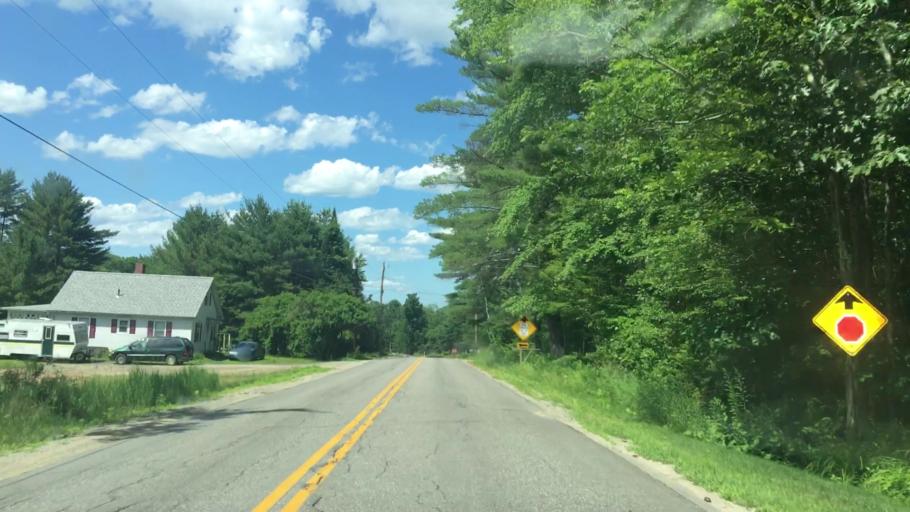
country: US
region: Maine
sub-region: Franklin County
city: Chesterville
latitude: 44.6141
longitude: -70.0814
